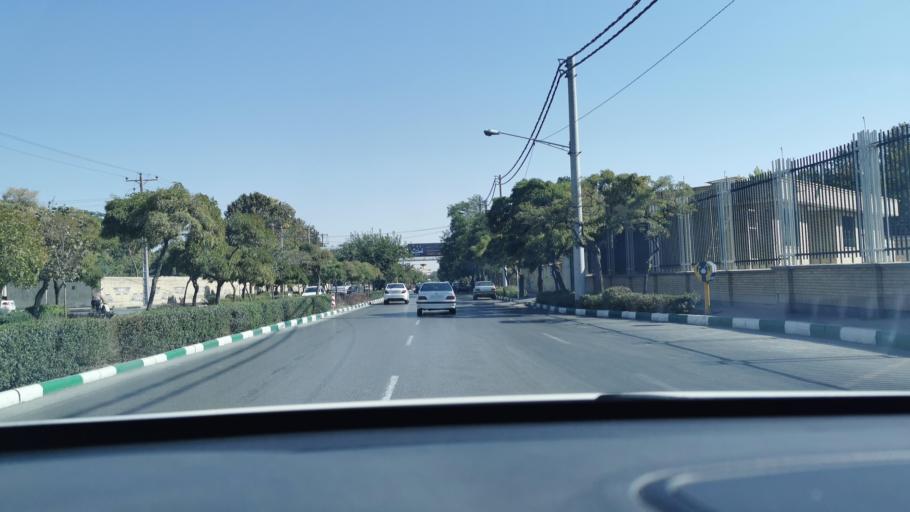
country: IR
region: Razavi Khorasan
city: Mashhad
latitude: 36.3277
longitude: 59.5818
